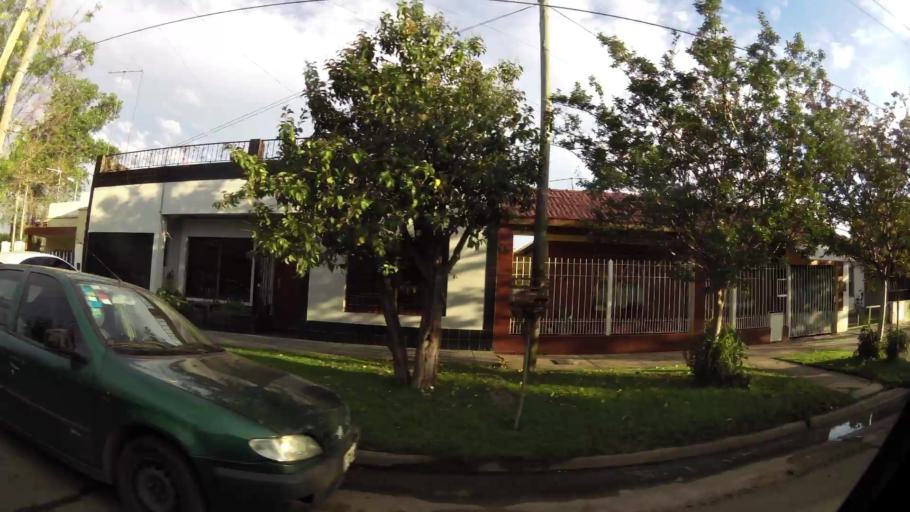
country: AR
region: Buenos Aires
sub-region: Partido de Almirante Brown
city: Adrogue
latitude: -34.7630
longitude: -58.3550
